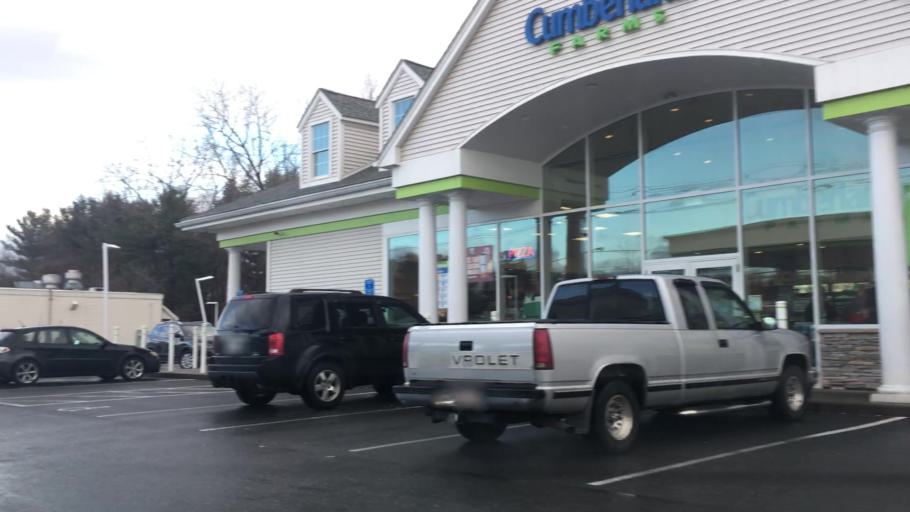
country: US
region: Massachusetts
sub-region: Hampden County
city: Agawam
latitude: 42.0606
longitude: -72.6318
